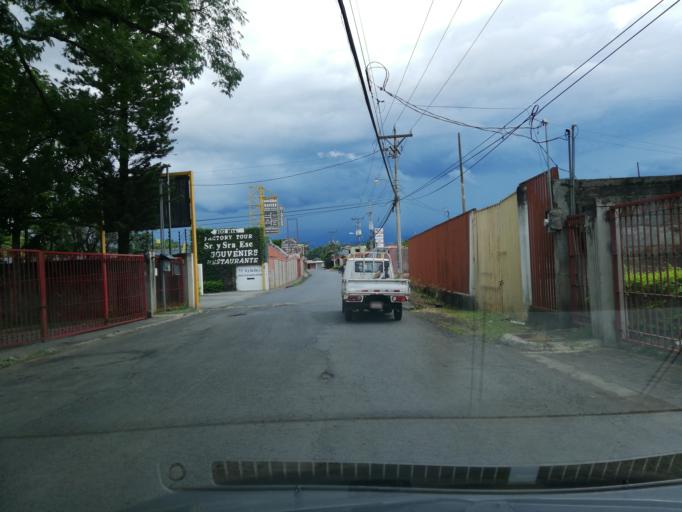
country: CR
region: Alajuela
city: Alajuela
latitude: 10.0000
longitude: -84.2249
